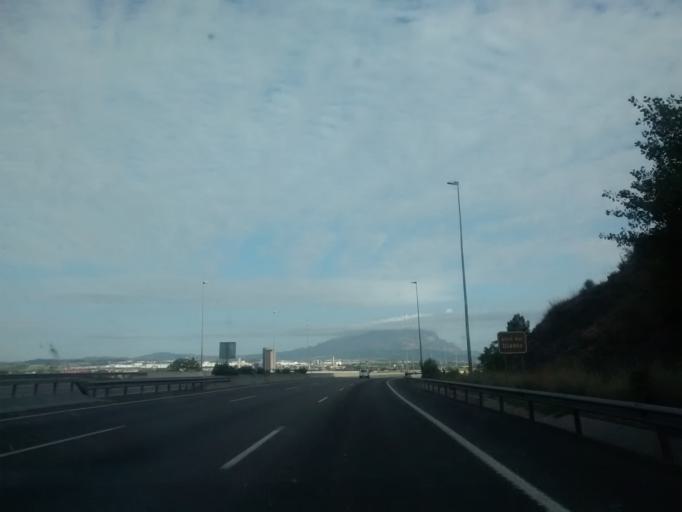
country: ES
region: Catalonia
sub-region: Provincia de Barcelona
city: Martorell
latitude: 41.4745
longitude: 1.9399
